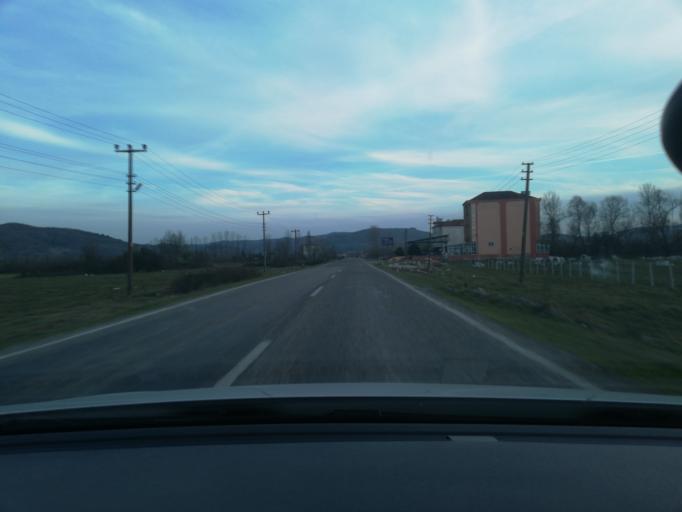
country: TR
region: Zonguldak
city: Saltukova
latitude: 41.5201
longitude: 32.1020
